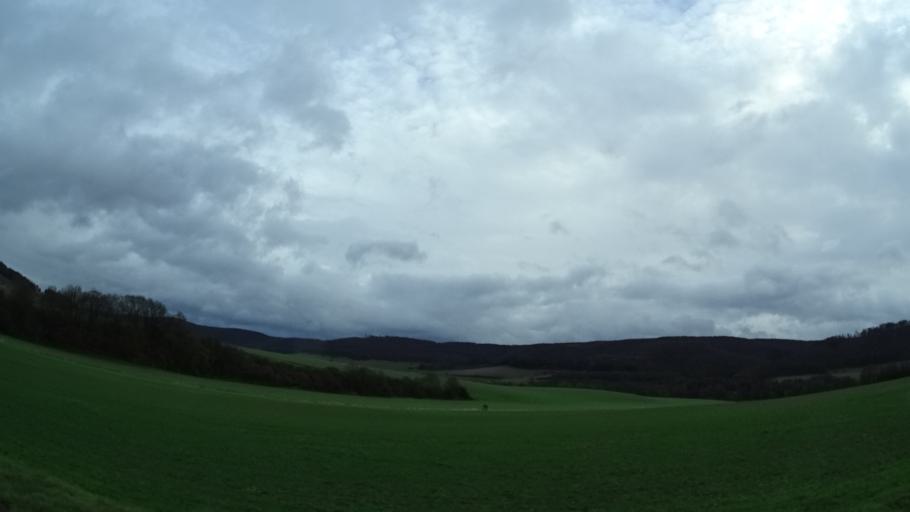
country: DE
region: Thuringia
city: Stepfershausen
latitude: 50.5639
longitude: 10.2991
